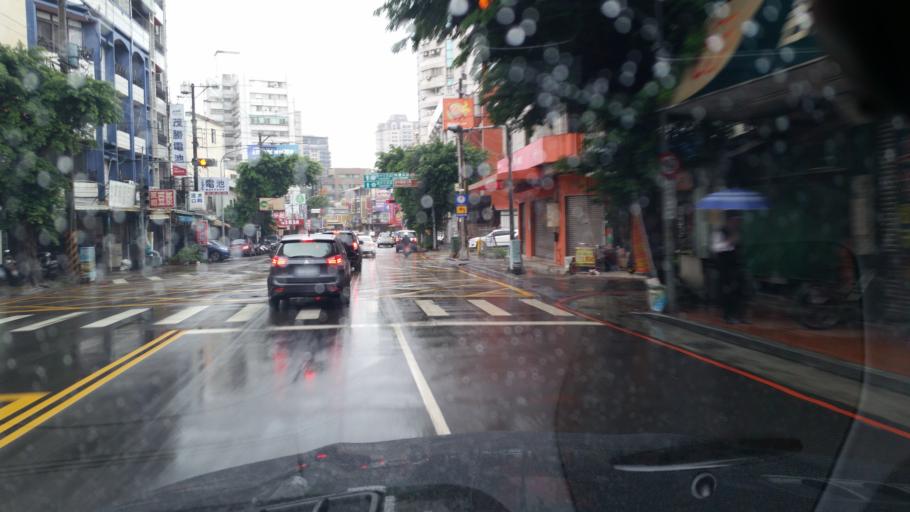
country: TW
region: Taiwan
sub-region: Taichung City
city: Taichung
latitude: 24.1816
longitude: 120.6385
